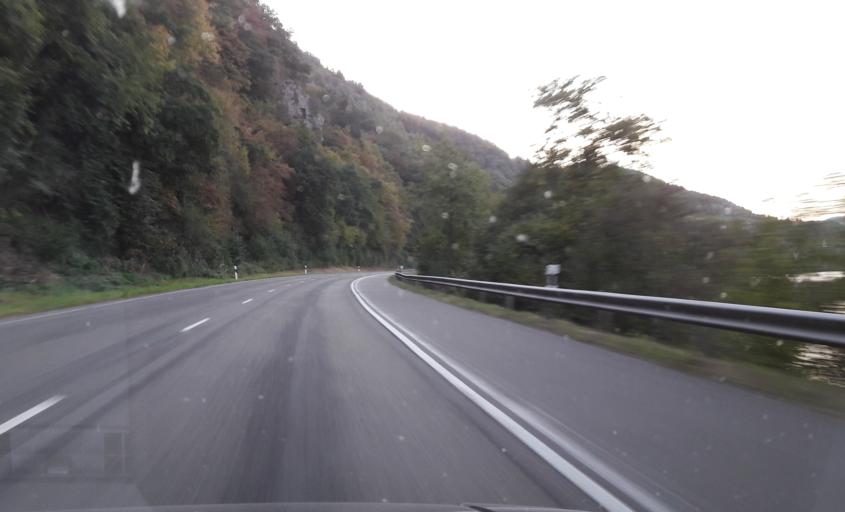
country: DE
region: Rheinland-Pfalz
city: Briedel
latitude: 50.0139
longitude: 7.1586
